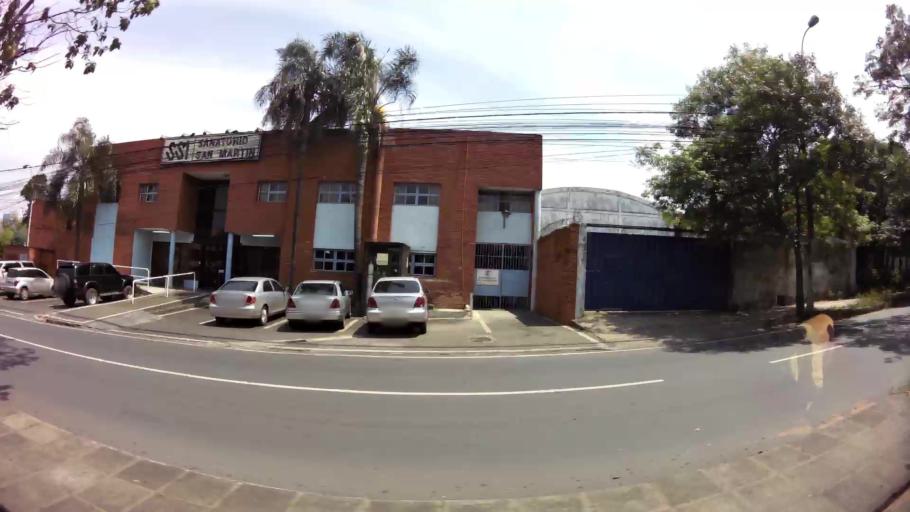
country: PY
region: Central
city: Lambare
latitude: -25.3201
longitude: -57.5930
